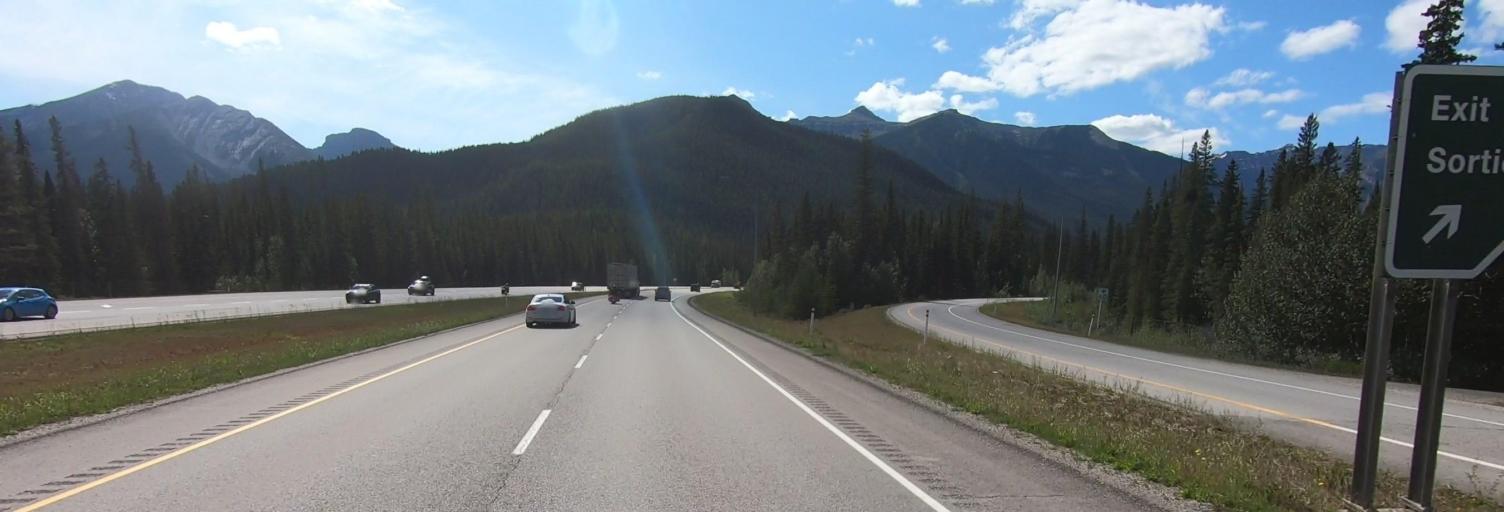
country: CA
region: Alberta
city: Banff
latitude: 51.1588
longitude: -115.6791
